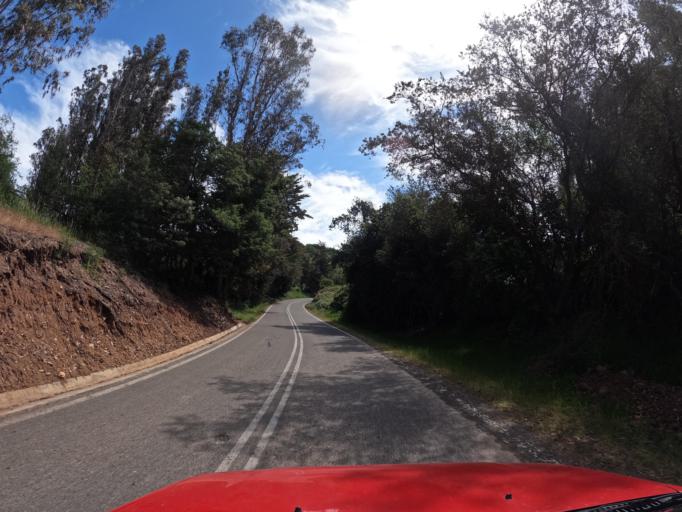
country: CL
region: Maule
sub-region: Provincia de Talca
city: Talca
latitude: -35.0072
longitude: -71.9751
